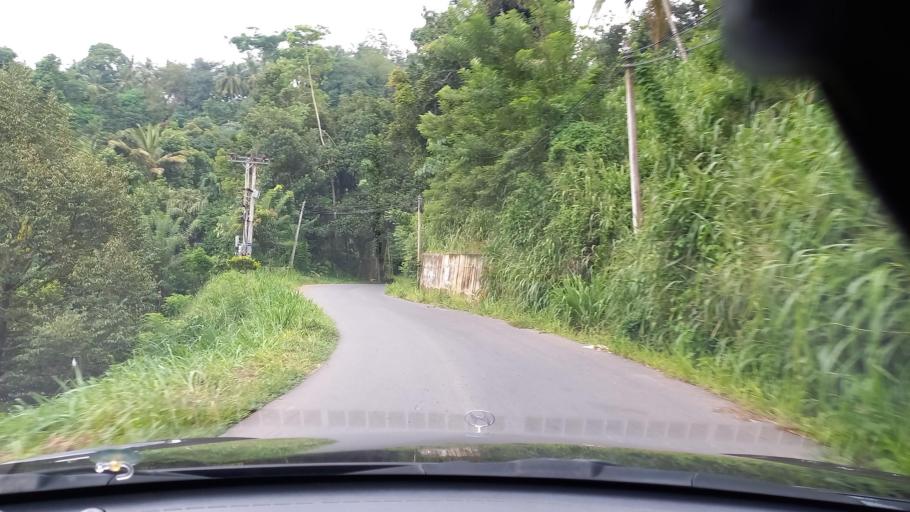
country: LK
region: Central
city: Gampola
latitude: 7.2095
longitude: 80.6246
